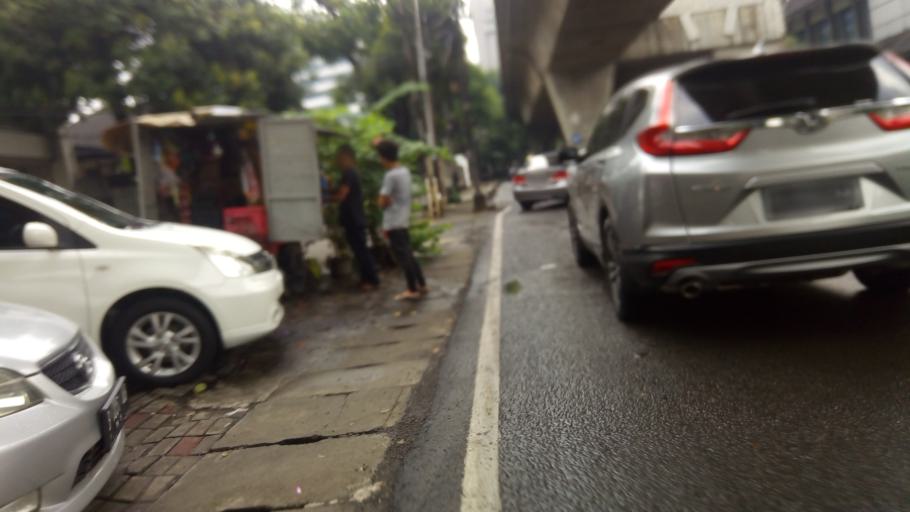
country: ID
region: Jakarta Raya
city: Jakarta
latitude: -6.2395
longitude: 106.8062
